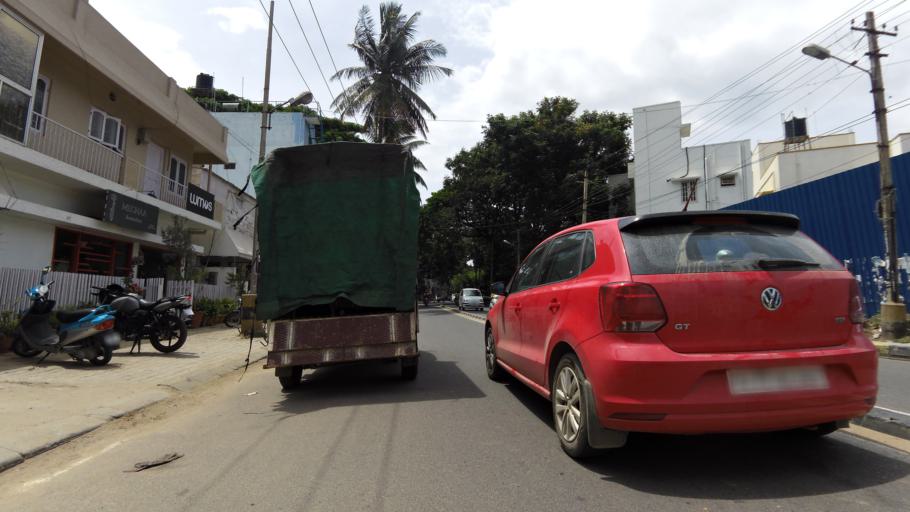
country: IN
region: Karnataka
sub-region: Bangalore Urban
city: Bangalore
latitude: 12.9678
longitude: 77.6365
